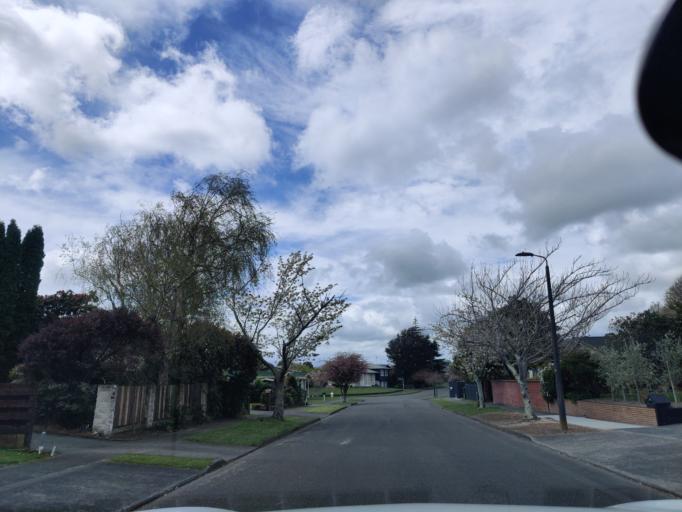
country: NZ
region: Manawatu-Wanganui
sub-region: Palmerston North City
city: Palmerston North
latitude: -40.3811
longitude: 175.5926
